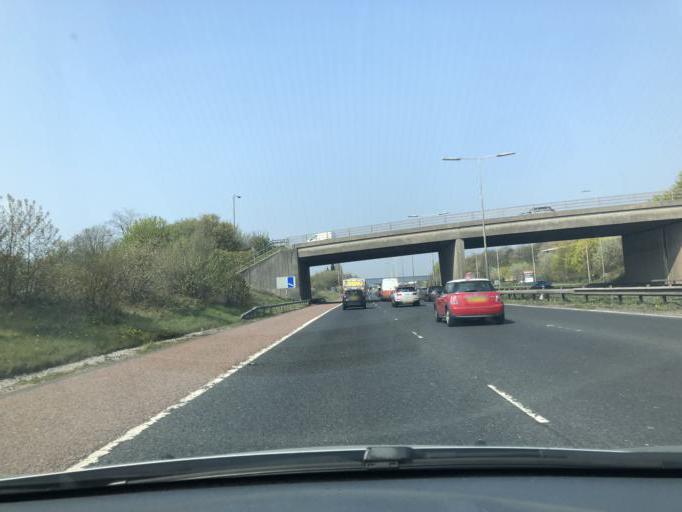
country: GB
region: England
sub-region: Borough of Tameside
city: Denton
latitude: 53.4490
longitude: -2.1351
